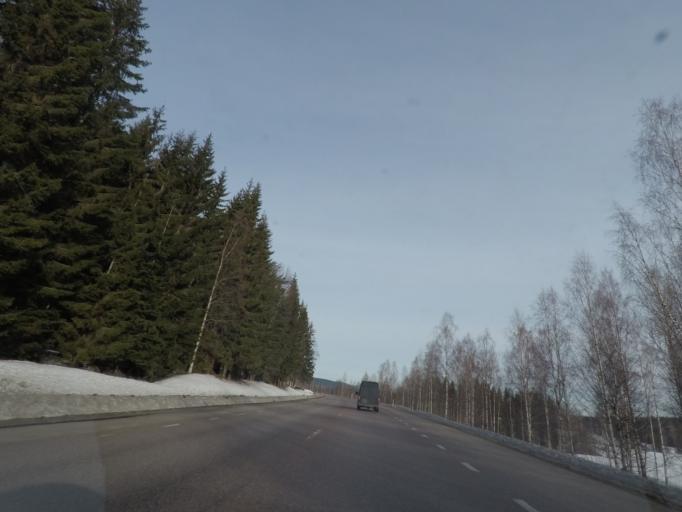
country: SE
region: Dalarna
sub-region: Smedjebackens Kommun
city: Smedjebacken
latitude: 60.1230
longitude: 15.4719
